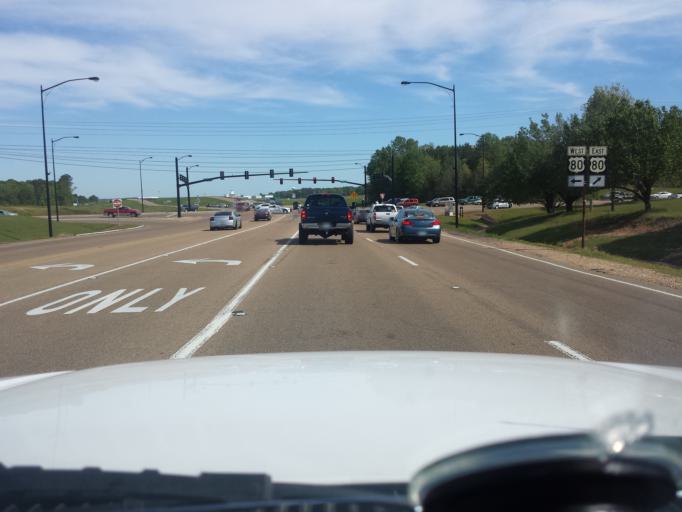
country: US
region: Mississippi
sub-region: Rankin County
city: Pearl
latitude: 32.2827
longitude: -90.0742
